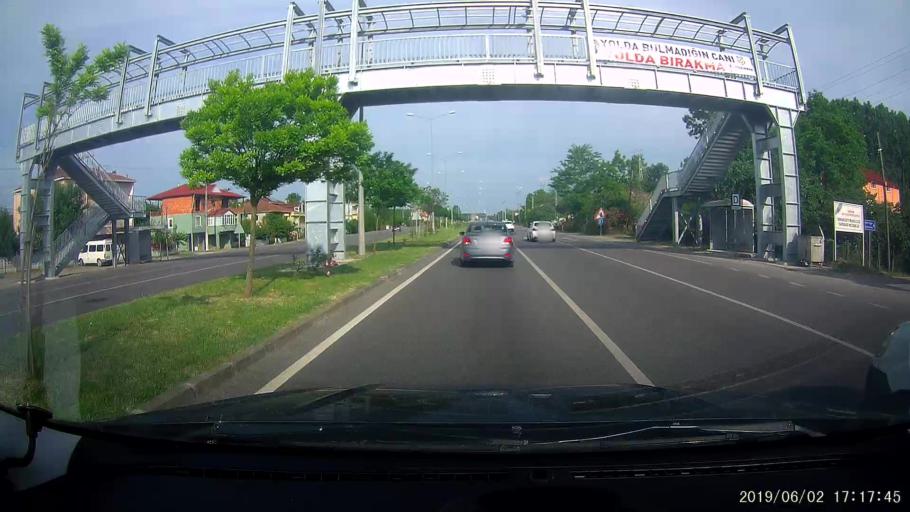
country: TR
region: Samsun
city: Dikbiyik
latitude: 41.2271
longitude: 36.5865
